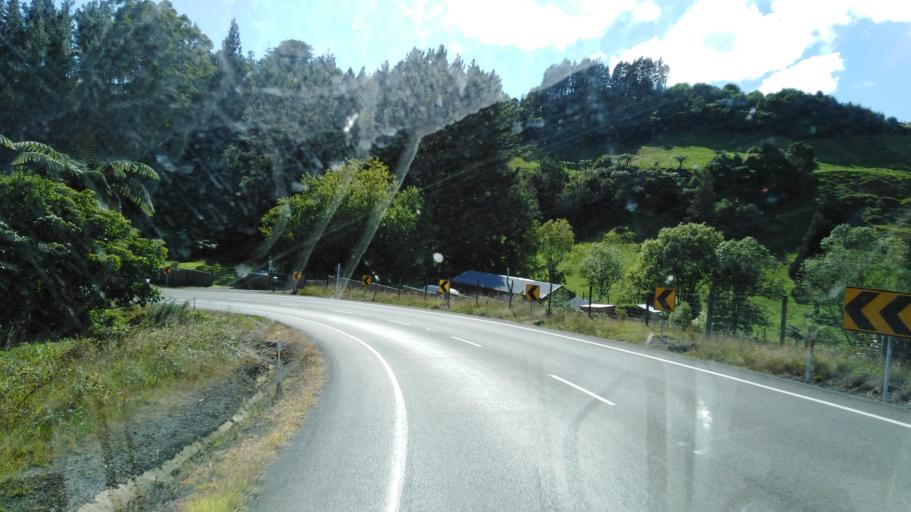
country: NZ
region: Bay of Plenty
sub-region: Tauranga City
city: Tauranga
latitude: -37.8296
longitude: 176.1256
